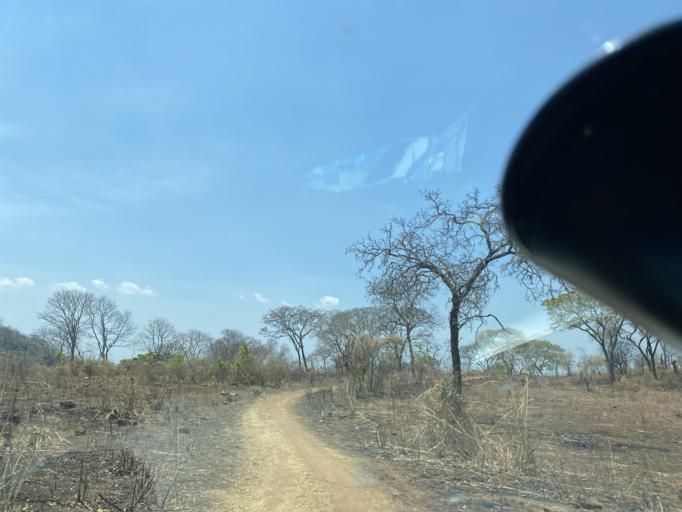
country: ZM
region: Lusaka
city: Kafue
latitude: -15.8049
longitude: 28.4456
